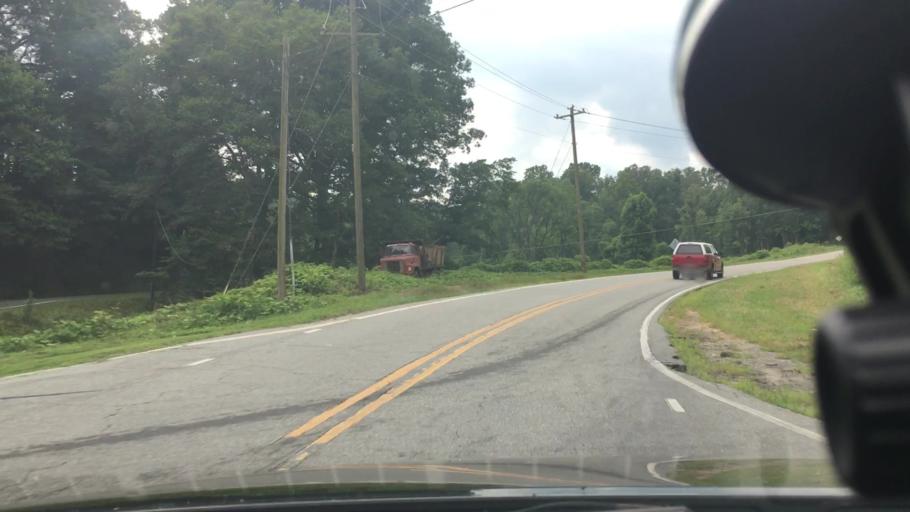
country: US
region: North Carolina
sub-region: McDowell County
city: West Marion
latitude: 35.6543
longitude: -82.0150
